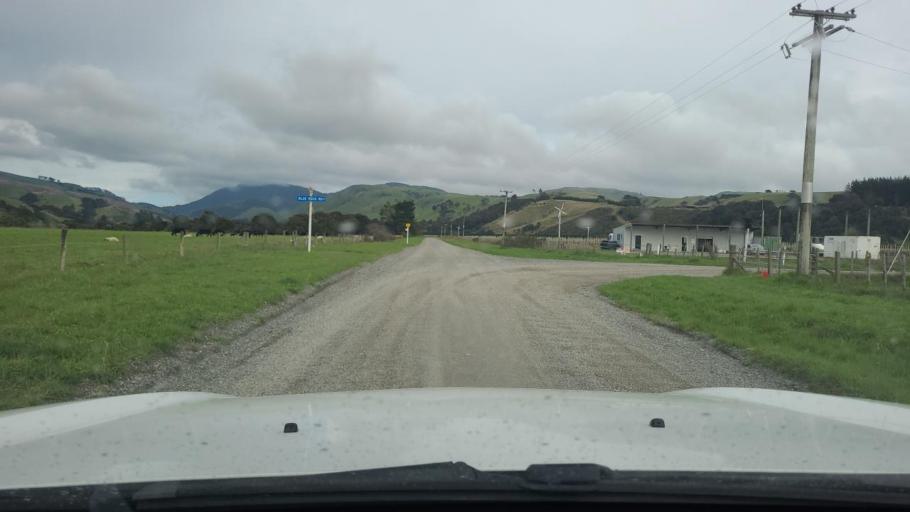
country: NZ
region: Wellington
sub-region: South Wairarapa District
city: Waipawa
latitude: -41.3274
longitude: 175.4275
